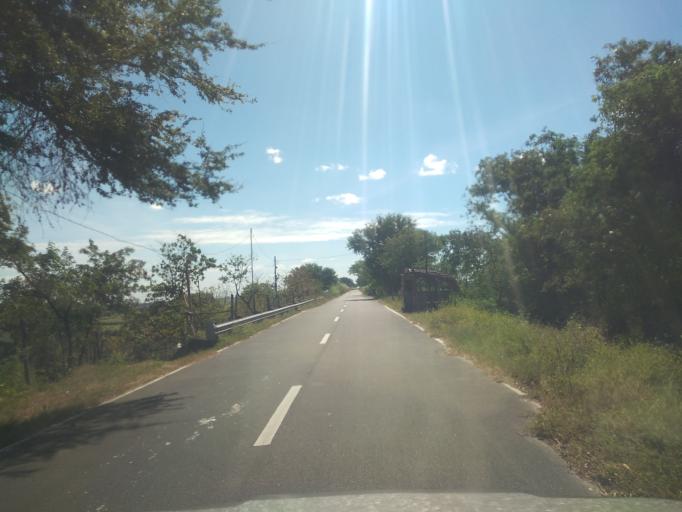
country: PH
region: Central Luzon
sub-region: Province of Pampanga
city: Balas
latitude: 15.0410
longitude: 120.5942
